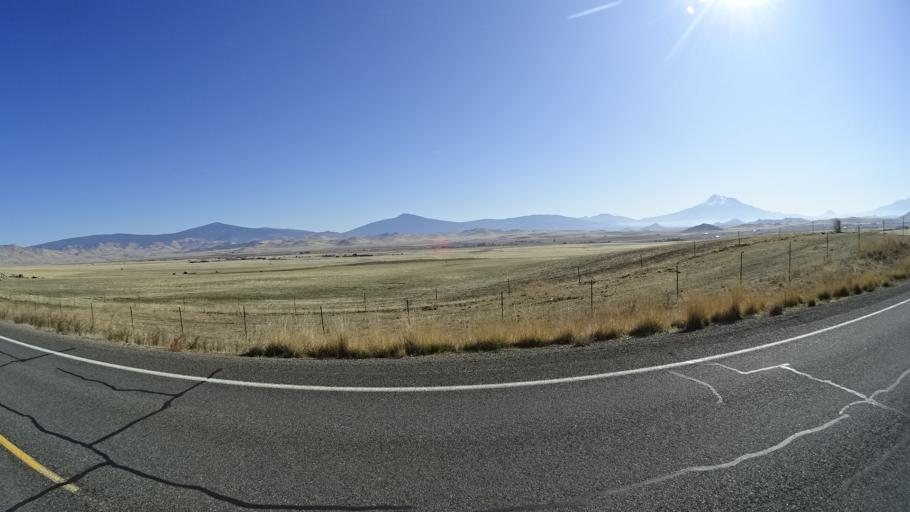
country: US
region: California
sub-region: Siskiyou County
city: Montague
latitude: 41.7835
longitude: -122.5188
